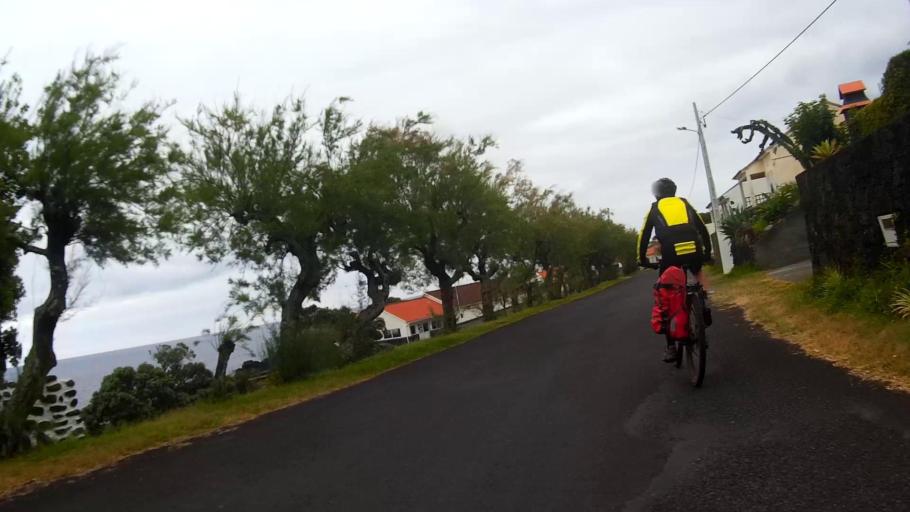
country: PT
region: Azores
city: Ribeira Grande
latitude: 38.5660
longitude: -28.7729
